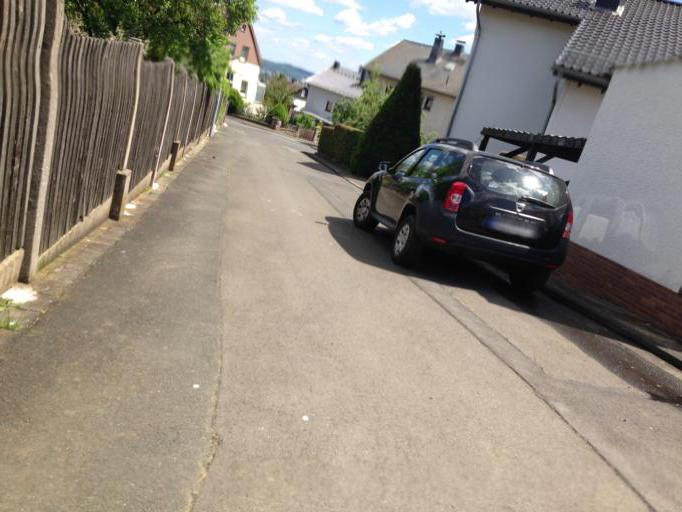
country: DE
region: Hesse
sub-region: Regierungsbezirk Giessen
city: Heuchelheim
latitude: 50.5929
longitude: 8.6141
